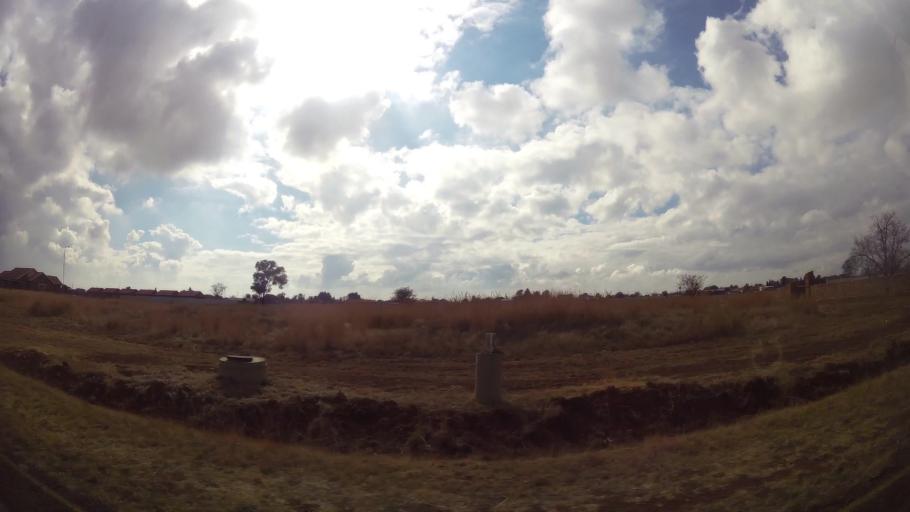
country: ZA
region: Gauteng
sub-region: Sedibeng District Municipality
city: Meyerton
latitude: -26.6132
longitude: 28.0504
